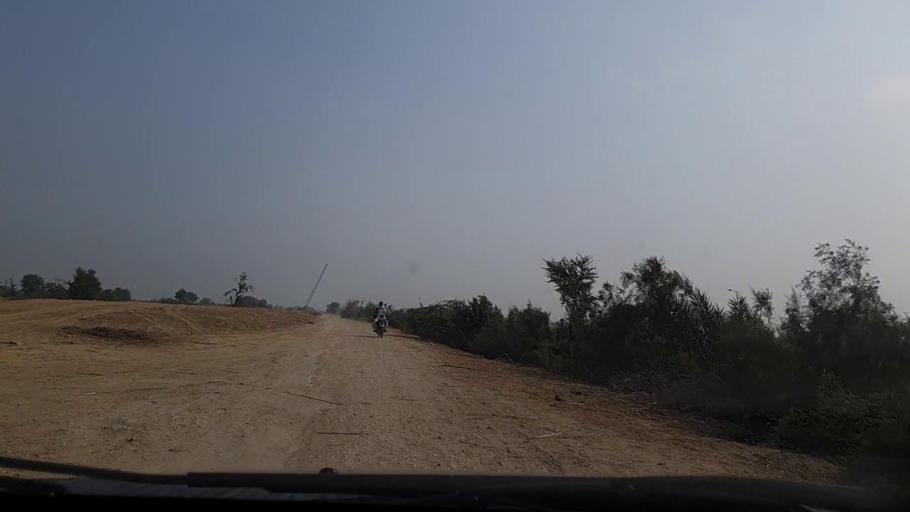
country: PK
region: Sindh
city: Sanghar
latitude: 26.0543
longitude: 68.9705
